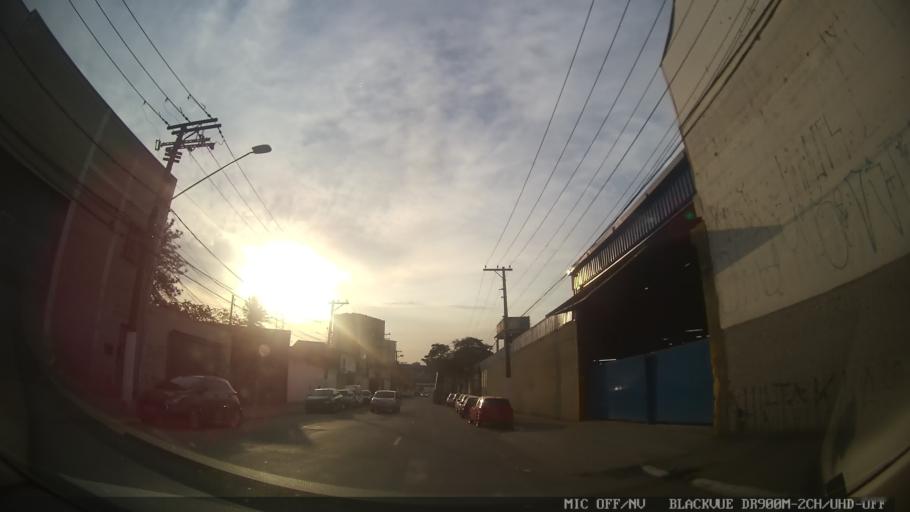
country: BR
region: Sao Paulo
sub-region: Sao Caetano Do Sul
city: Sao Caetano do Sul
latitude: -23.5998
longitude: -46.5952
